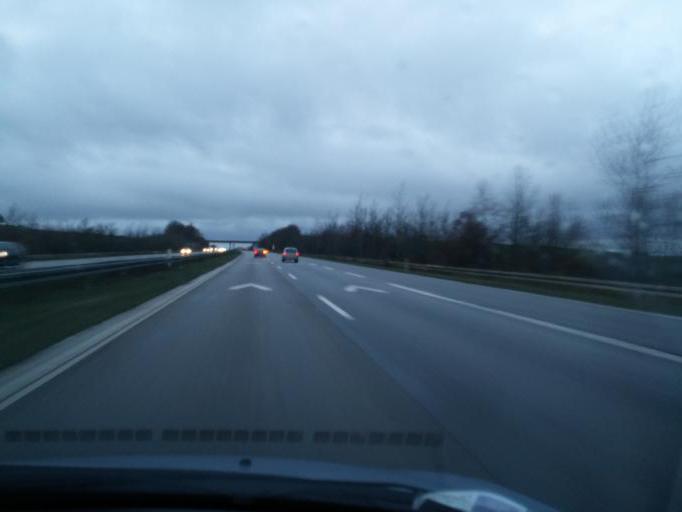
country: DK
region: South Denmark
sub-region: Assens Kommune
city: Vissenbjerg
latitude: 55.4032
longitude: 10.1488
